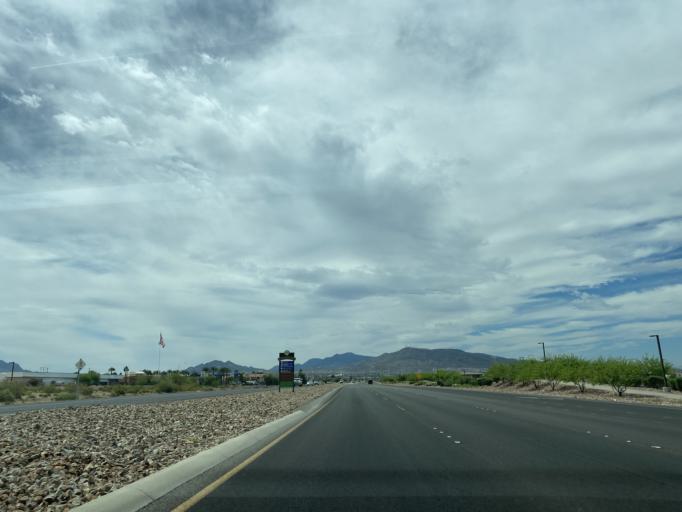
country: US
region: Nevada
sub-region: Clark County
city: Henderson
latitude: 36.0617
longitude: -114.9636
